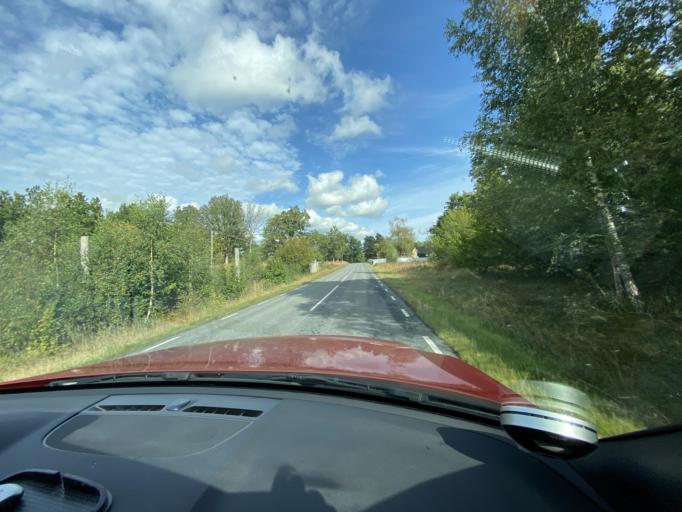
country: SE
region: Skane
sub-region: Hassleholms Kommun
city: Bjarnum
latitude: 56.3521
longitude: 13.7345
